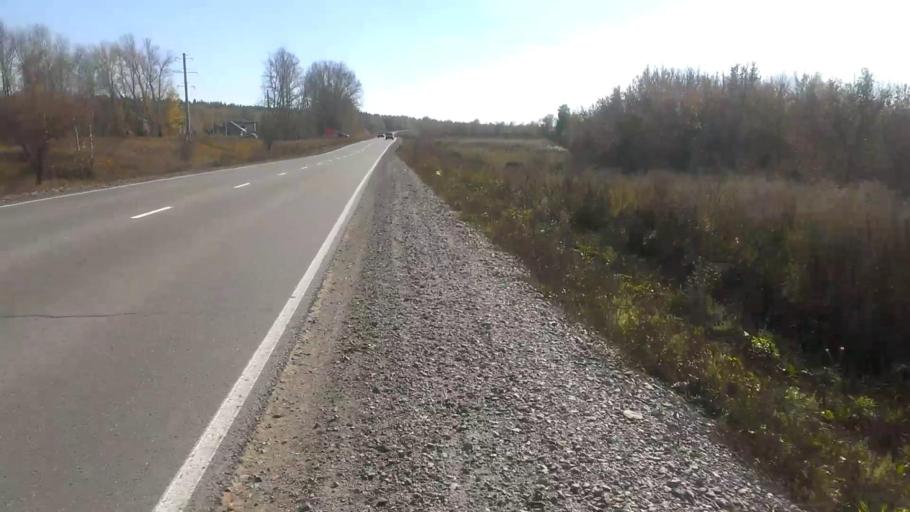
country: RU
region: Altai Krai
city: Sannikovo
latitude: 53.3093
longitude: 83.9670
